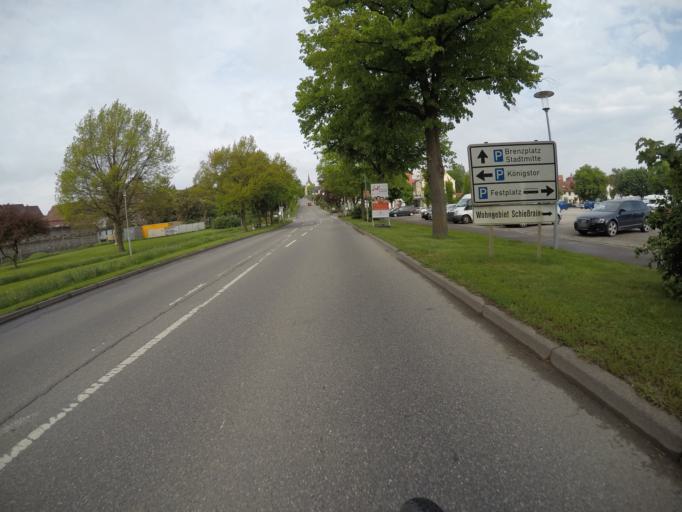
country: DE
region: Baden-Wuerttemberg
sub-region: Regierungsbezirk Stuttgart
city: Weil der Stadt
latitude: 48.7520
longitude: 8.8751
